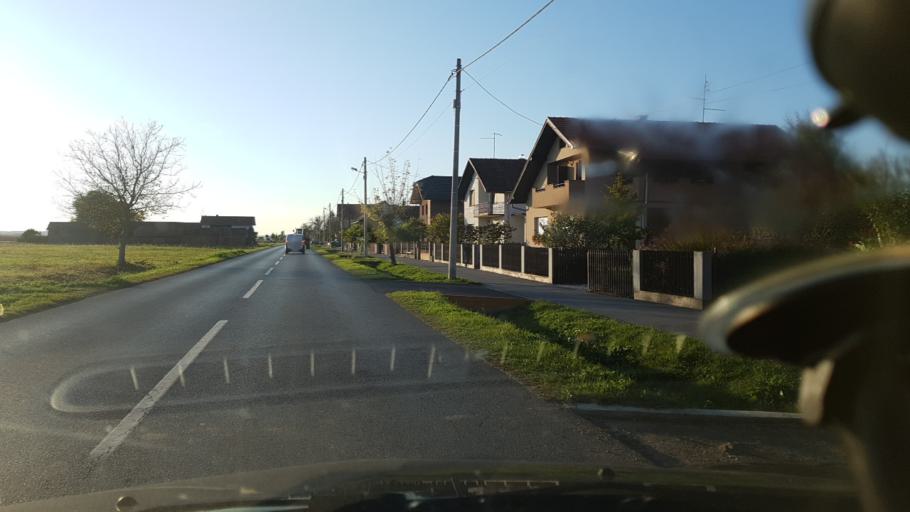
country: HR
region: Koprivnicko-Krizevacka
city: Virje
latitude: 46.0482
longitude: 17.0426
